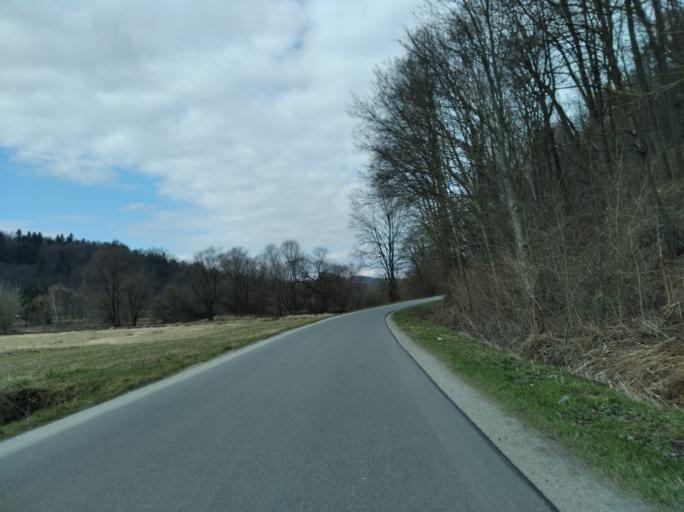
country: PL
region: Subcarpathian Voivodeship
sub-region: Powiat strzyzowski
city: Frysztak
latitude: 49.8512
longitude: 21.6244
